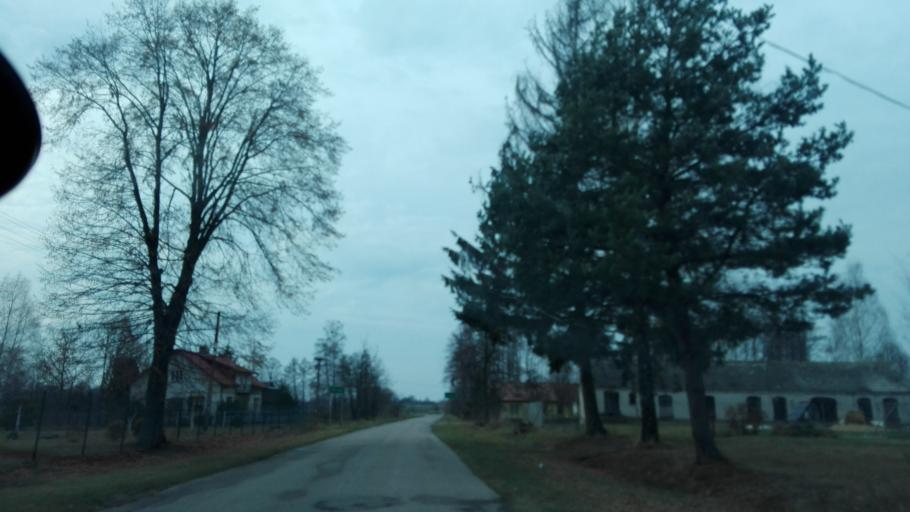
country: PL
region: Lublin Voivodeship
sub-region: Powiat bialski
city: Sosnowka
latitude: 51.7247
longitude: 23.4427
